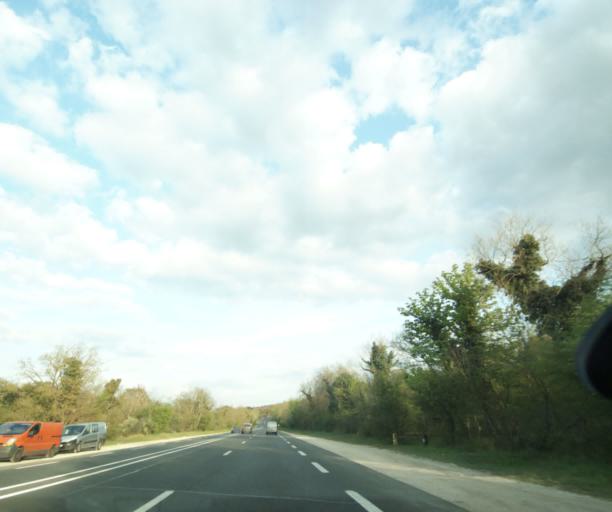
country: FR
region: Ile-de-France
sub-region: Departement de Seine-et-Marne
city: Barbizon
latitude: 48.4437
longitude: 2.6430
